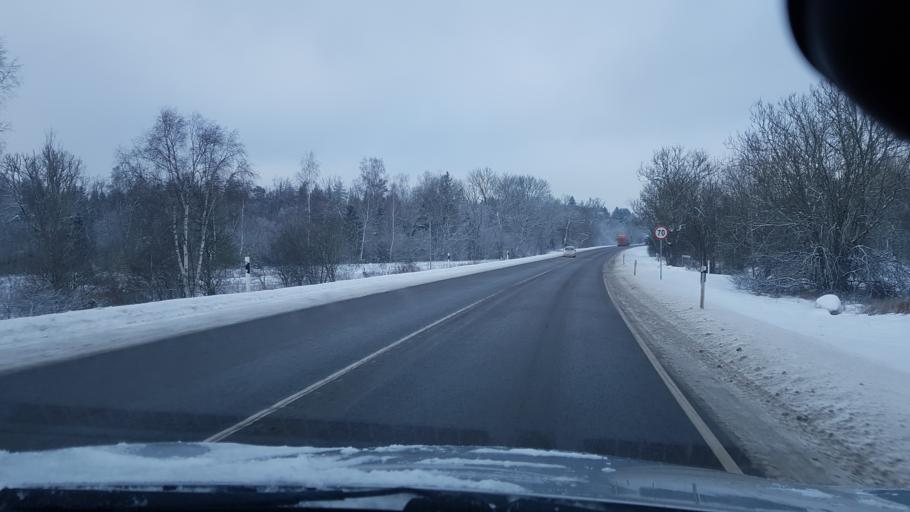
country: EE
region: Harju
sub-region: Keila linn
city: Keila
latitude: 59.3371
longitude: 24.2765
